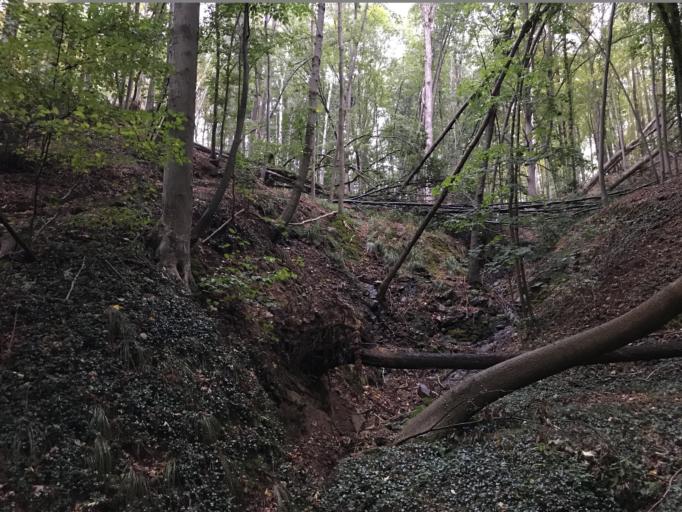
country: DE
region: Saxony
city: Seelitz
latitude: 51.0229
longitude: 12.8374
